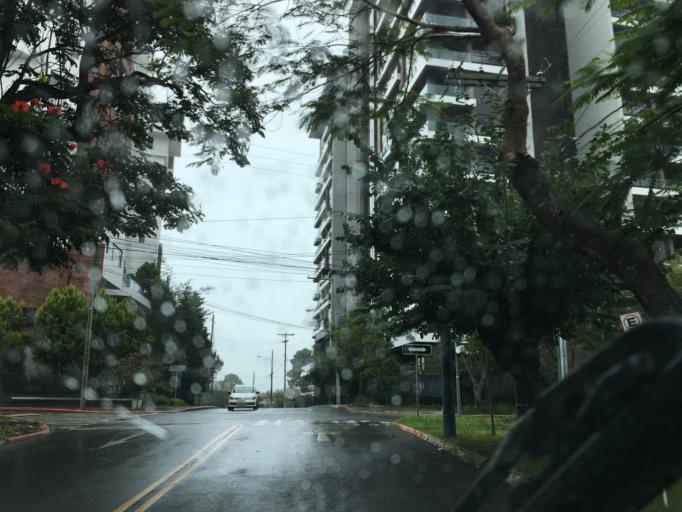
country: GT
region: Guatemala
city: Santa Catarina Pinula
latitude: 14.5842
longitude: -90.4886
